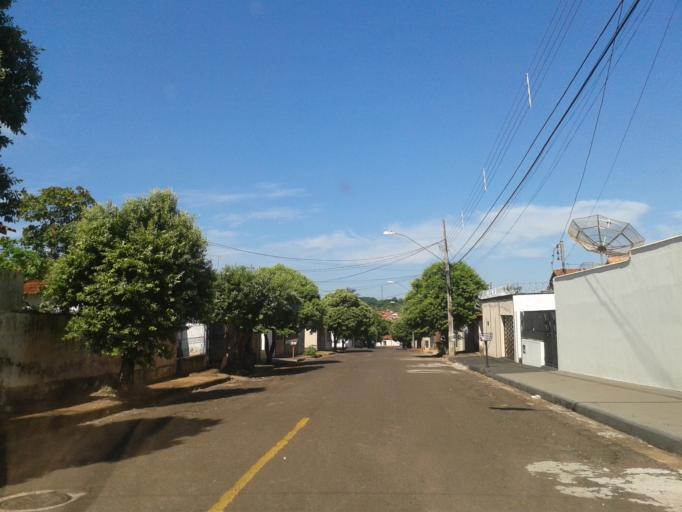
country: BR
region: Minas Gerais
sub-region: Ituiutaba
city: Ituiutaba
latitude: -18.9824
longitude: -49.4703
